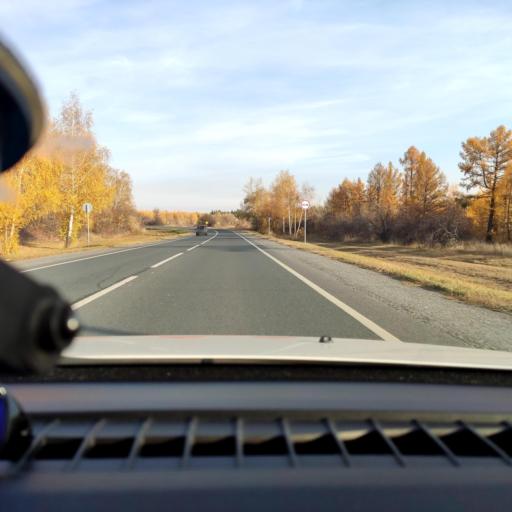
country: RU
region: Samara
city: Volzhskiy
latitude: 53.4639
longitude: 50.1277
